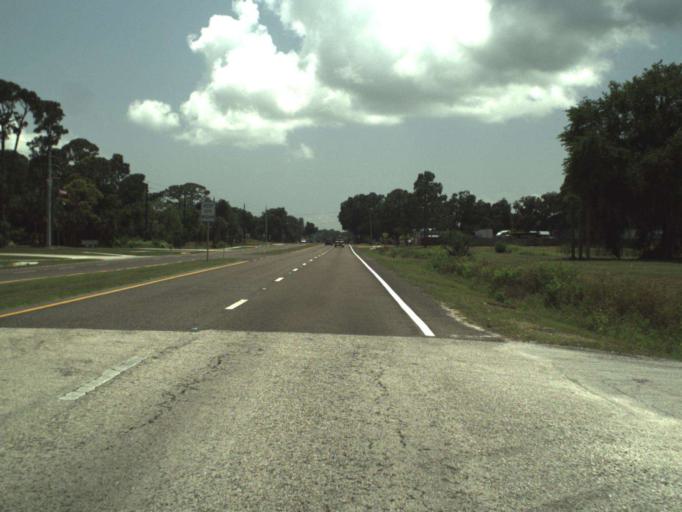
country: US
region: Florida
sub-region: Volusia County
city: Oak Hill
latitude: 28.8715
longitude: -80.8516
